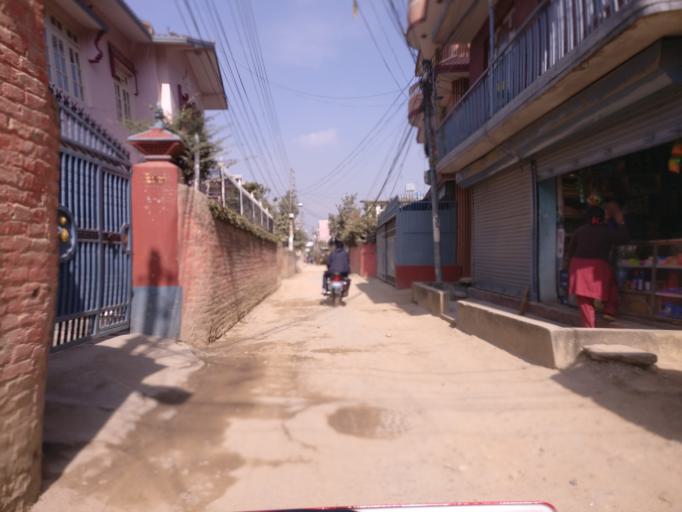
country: NP
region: Central Region
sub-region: Bagmati Zone
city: Patan
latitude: 27.6643
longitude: 85.3158
